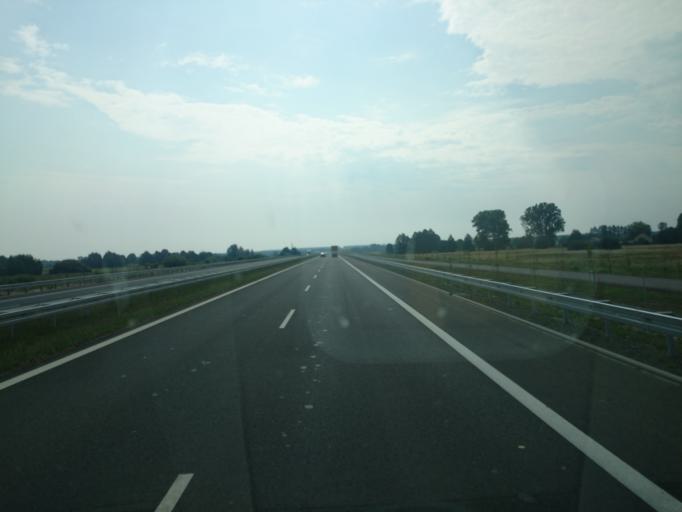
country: PL
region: Lubusz
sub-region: Powiat gorzowski
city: Deszczno
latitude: 52.6659
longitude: 15.3150
